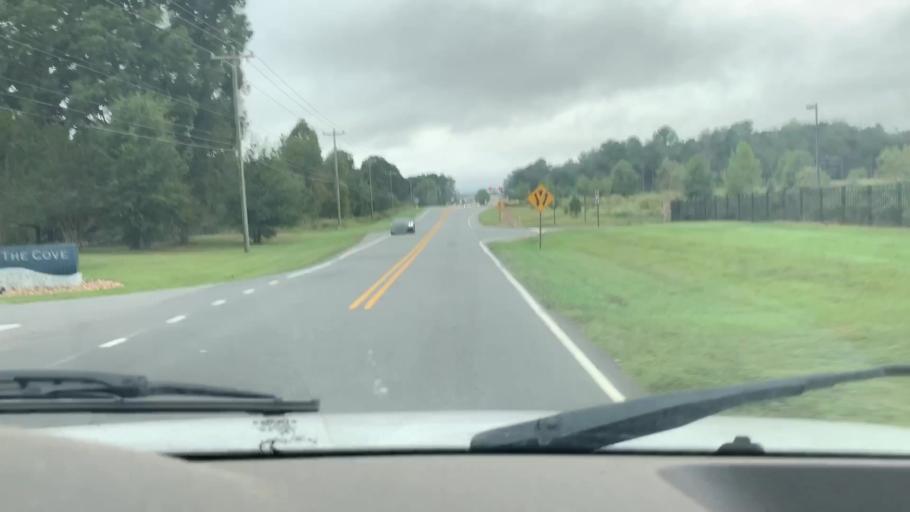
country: US
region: North Carolina
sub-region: Gaston County
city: Davidson
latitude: 35.5354
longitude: -80.8531
